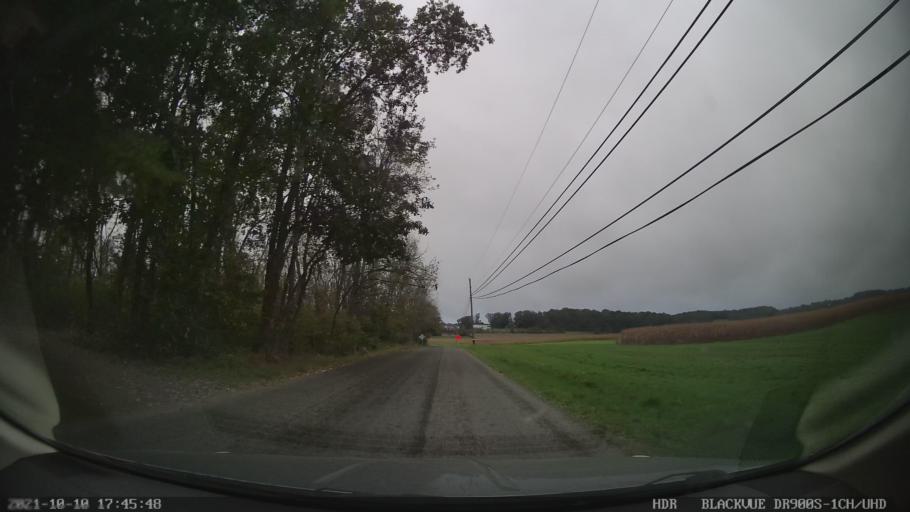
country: US
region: Pennsylvania
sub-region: Lehigh County
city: Breinigsville
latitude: 40.5551
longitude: -75.6759
